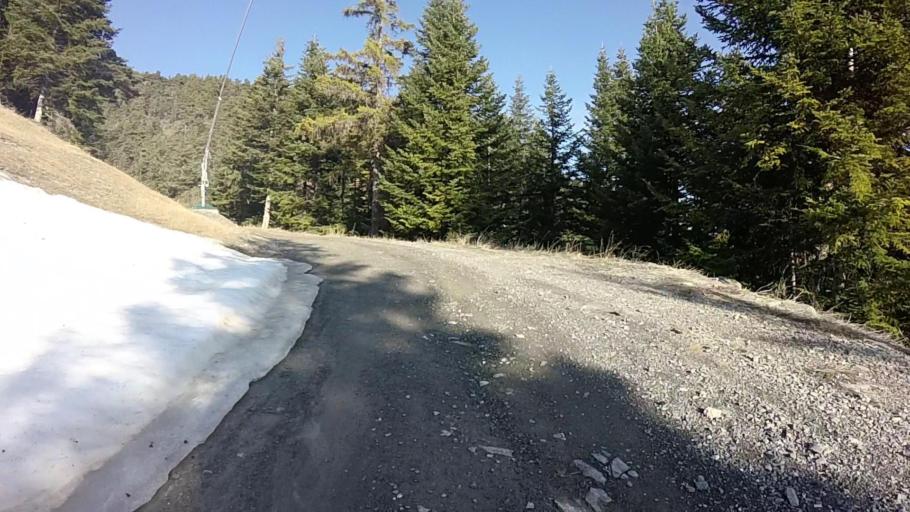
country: FR
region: Provence-Alpes-Cote d'Azur
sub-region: Departement des Alpes-de-Haute-Provence
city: Seyne-les-Alpes
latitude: 44.3471
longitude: 6.2858
